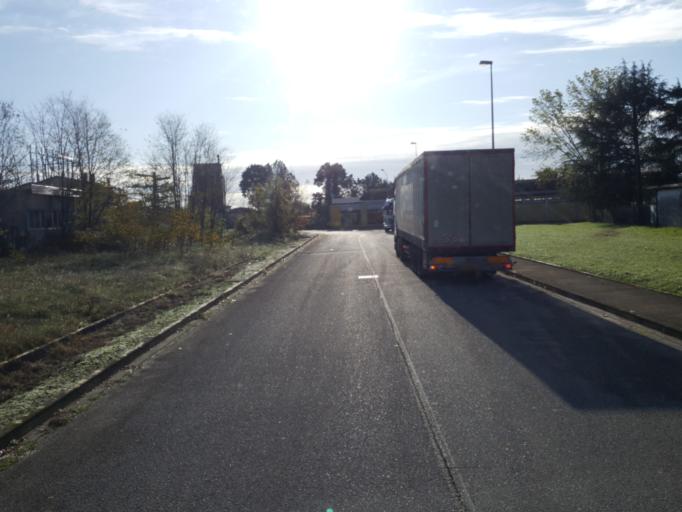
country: IT
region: Friuli Venezia Giulia
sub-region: Provincia di Udine
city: Manzano
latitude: 45.9873
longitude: 13.3662
